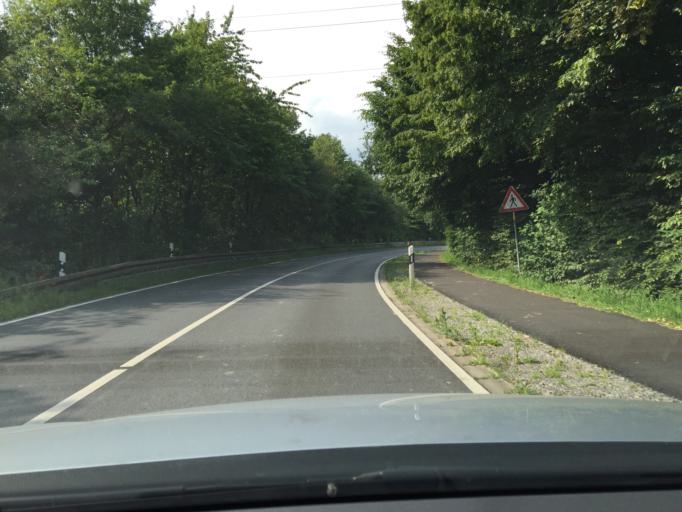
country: DE
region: North Rhine-Westphalia
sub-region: Regierungsbezirk Dusseldorf
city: Velbert
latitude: 51.3550
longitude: 7.0844
